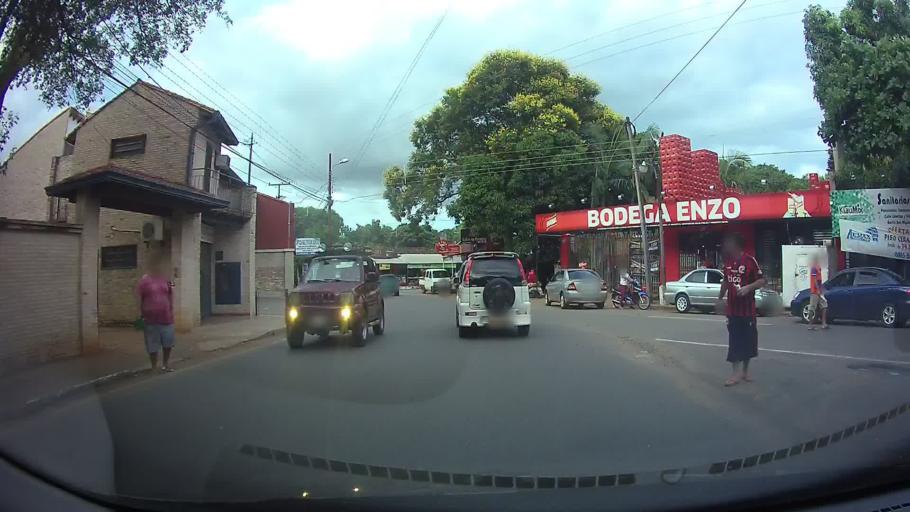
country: PY
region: Central
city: Fernando de la Mora
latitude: -25.3061
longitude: -57.5261
